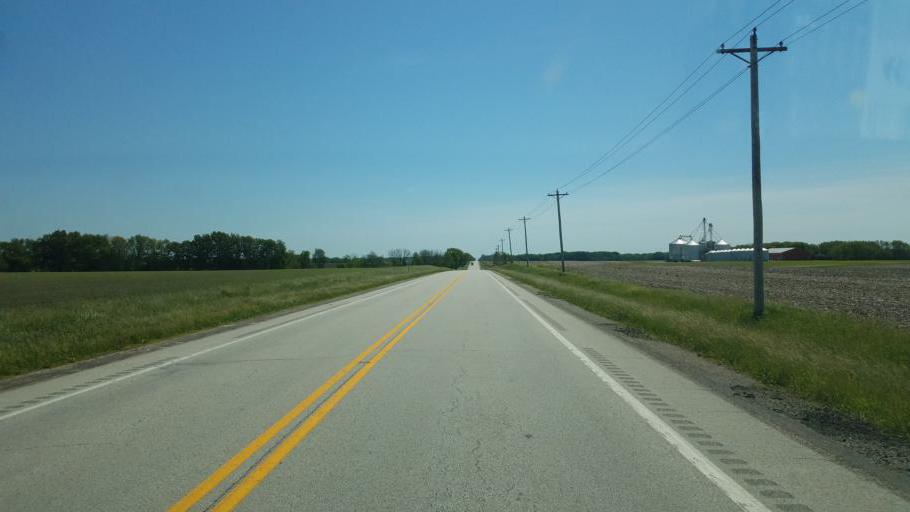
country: US
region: Illinois
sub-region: McLean County
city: Le Roy
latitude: 40.3117
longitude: -88.7920
